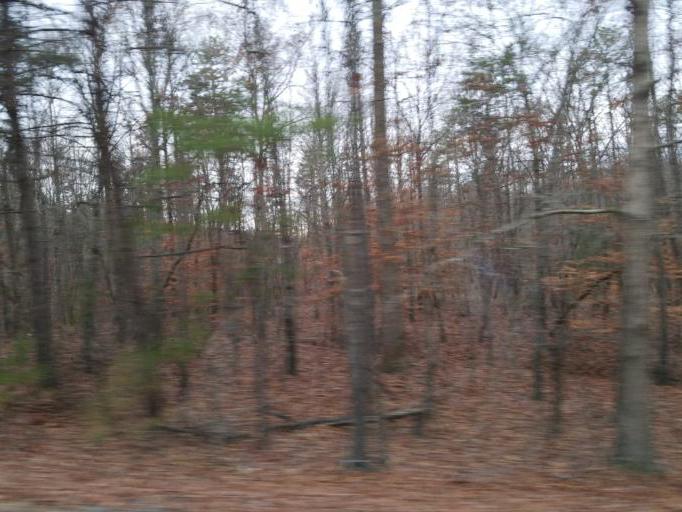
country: US
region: Georgia
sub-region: Dawson County
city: Dawsonville
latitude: 34.4047
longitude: -84.0150
